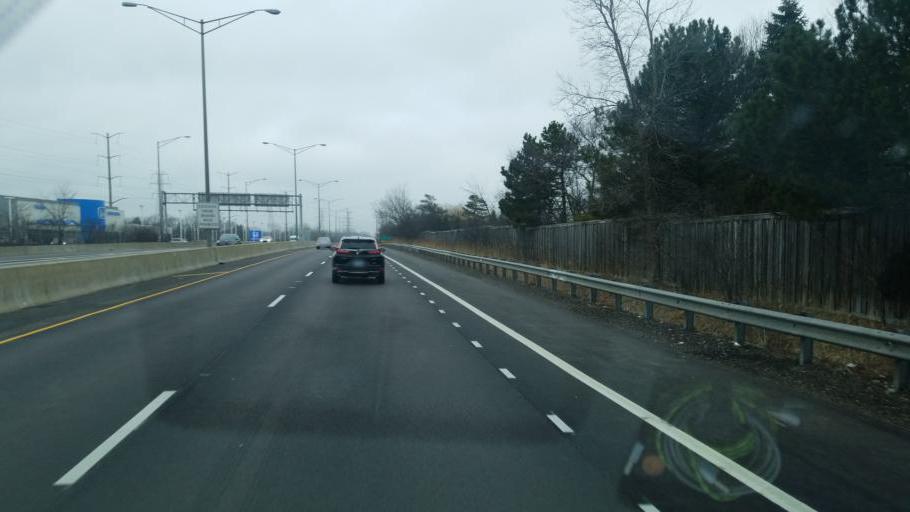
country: US
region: Illinois
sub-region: Lake County
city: Highland Park
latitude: 42.1616
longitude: -87.8076
